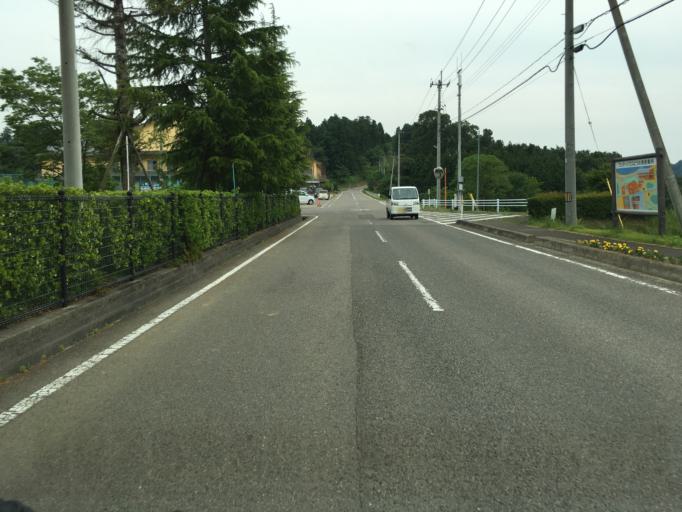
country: JP
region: Fukushima
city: Nihommatsu
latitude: 37.6306
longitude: 140.5259
